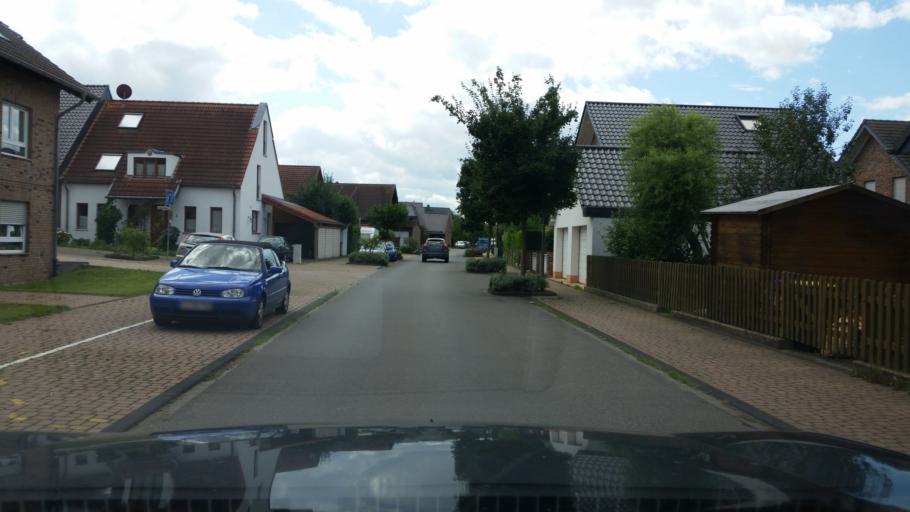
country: DE
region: North Rhine-Westphalia
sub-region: Regierungsbezirk Koln
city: Weilerswist
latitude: 50.7530
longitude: 6.8362
